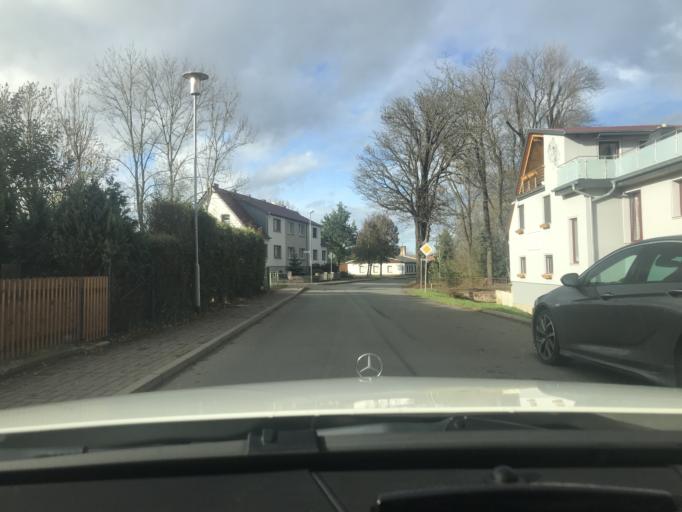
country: DE
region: Thuringia
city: Friemar
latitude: 50.9808
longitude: 10.7874
